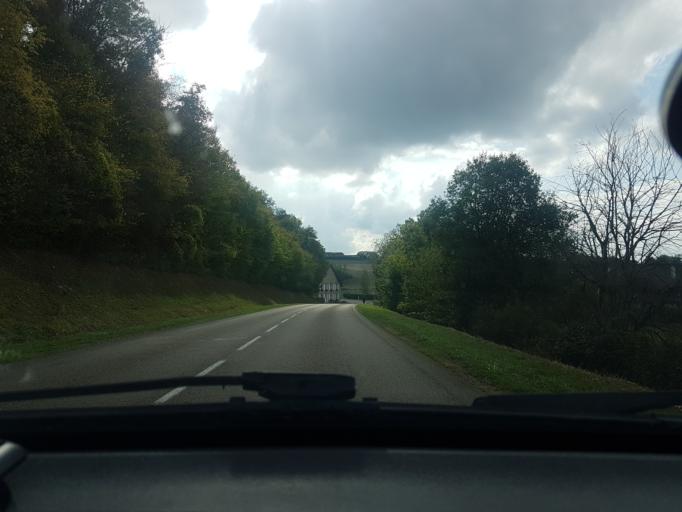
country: FR
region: Franche-Comte
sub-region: Departement du Doubs
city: Roulans
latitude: 47.4105
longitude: 6.2431
